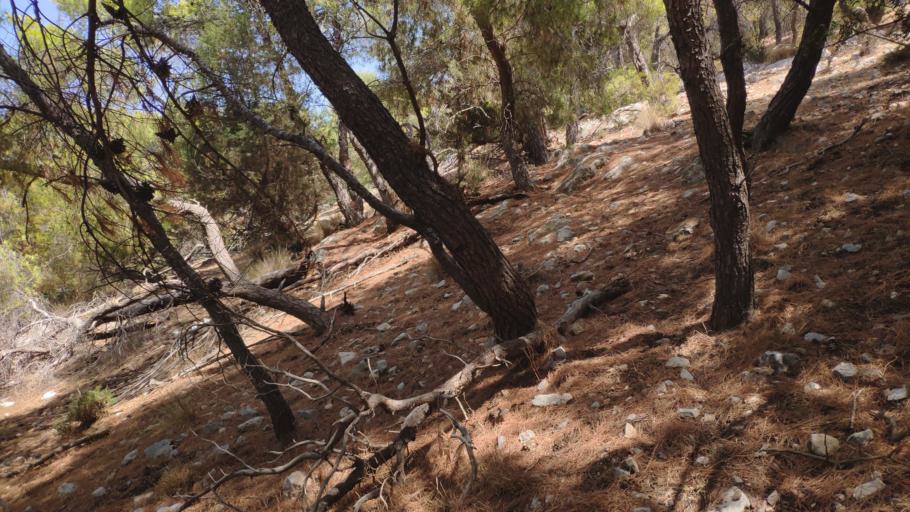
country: GR
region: Attica
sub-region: Nomos Piraios
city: Aegina
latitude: 37.6940
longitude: 23.4347
